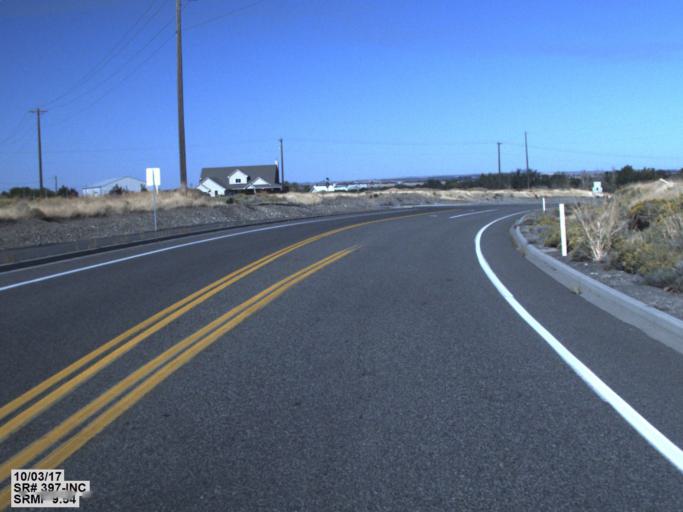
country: US
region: Washington
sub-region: Benton County
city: Finley
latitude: 46.1374
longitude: -119.0341
